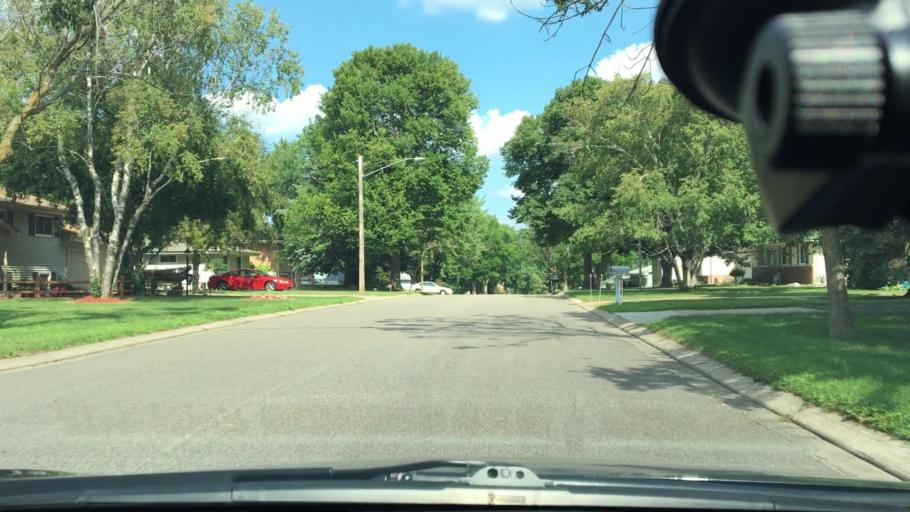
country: US
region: Minnesota
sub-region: Hennepin County
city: New Hope
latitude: 45.0378
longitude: -93.3880
